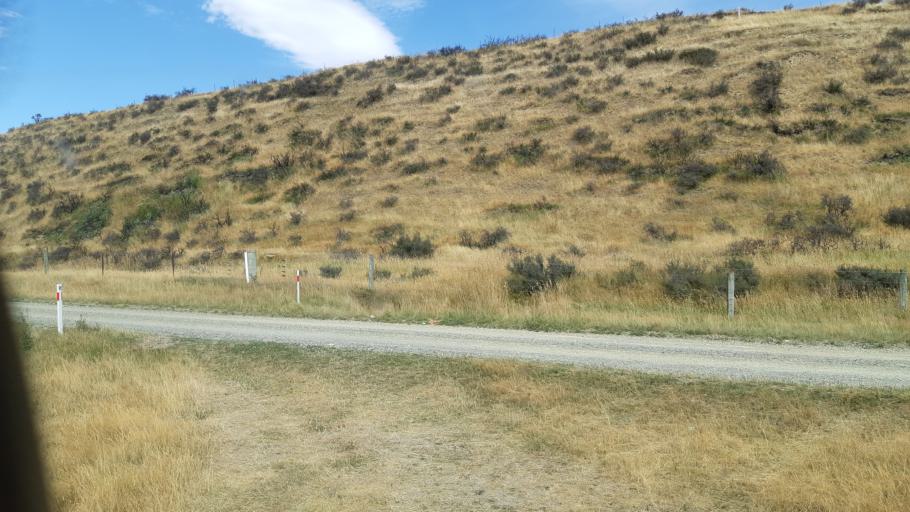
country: NZ
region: Canterbury
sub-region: Timaru District
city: Pleasant Point
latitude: -44.3767
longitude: 170.6490
